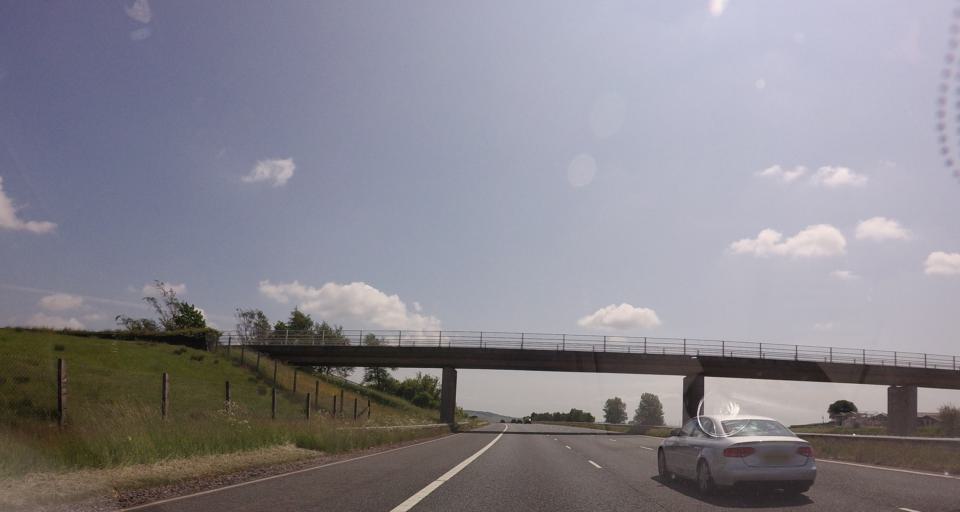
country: GB
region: Scotland
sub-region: Dumfries and Galloway
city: Lockerbie
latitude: 55.0779
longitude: -3.3110
